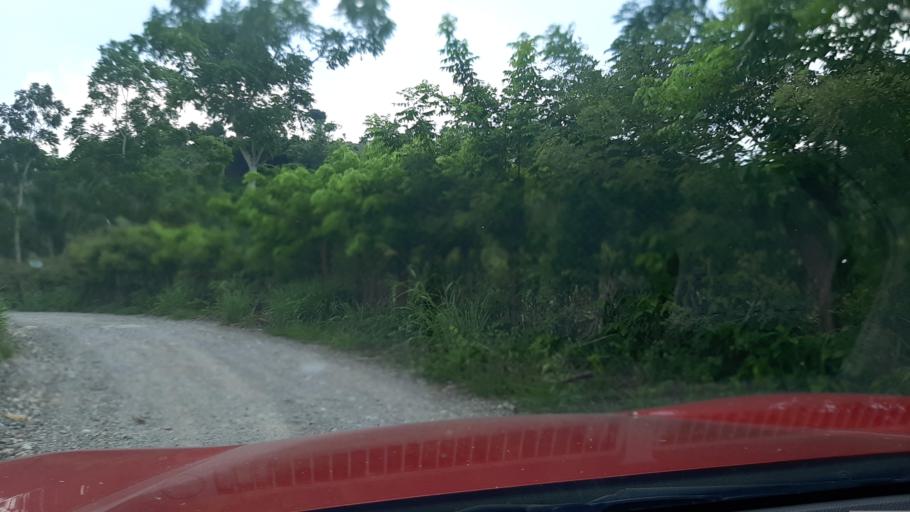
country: MX
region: Veracruz
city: Papantla de Olarte
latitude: 20.4181
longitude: -97.2776
